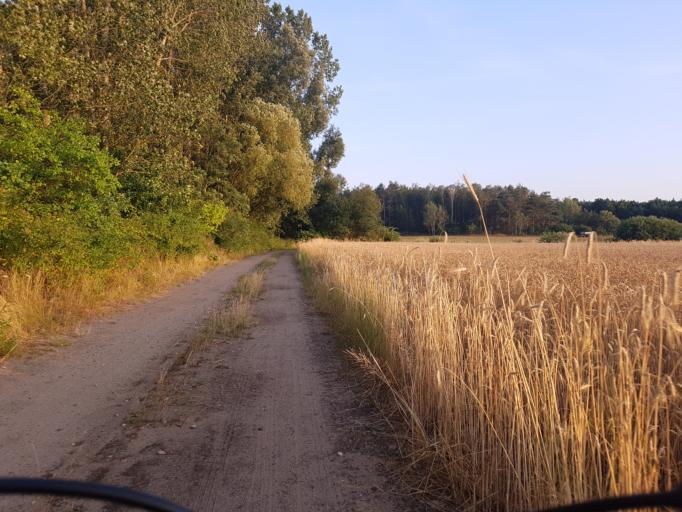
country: DE
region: Brandenburg
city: Bad Liebenwerda
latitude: 51.5609
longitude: 13.4054
